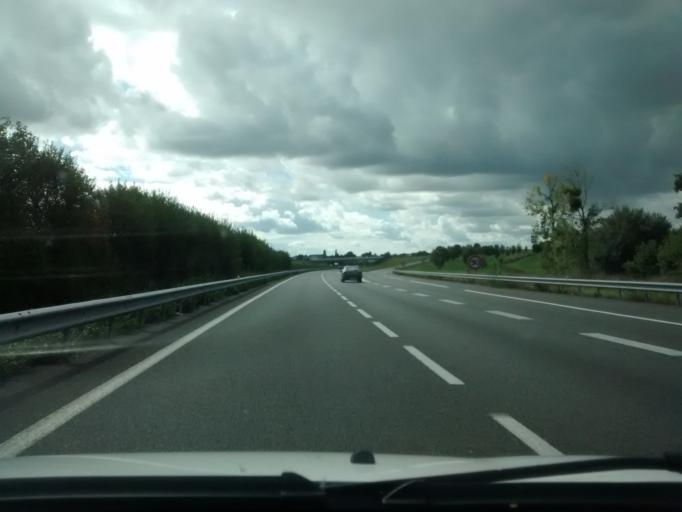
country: FR
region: Brittany
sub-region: Departement d'Ille-et-Vilaine
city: Liffre
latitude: 48.2246
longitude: -1.4947
